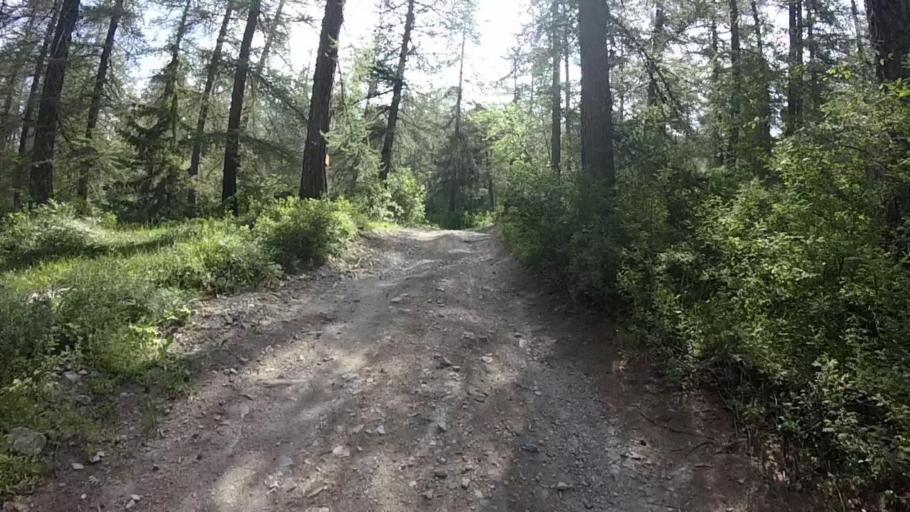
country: FR
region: Provence-Alpes-Cote d'Azur
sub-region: Departement des Alpes-de-Haute-Provence
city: Seyne-les-Alpes
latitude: 44.4042
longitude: 6.3613
